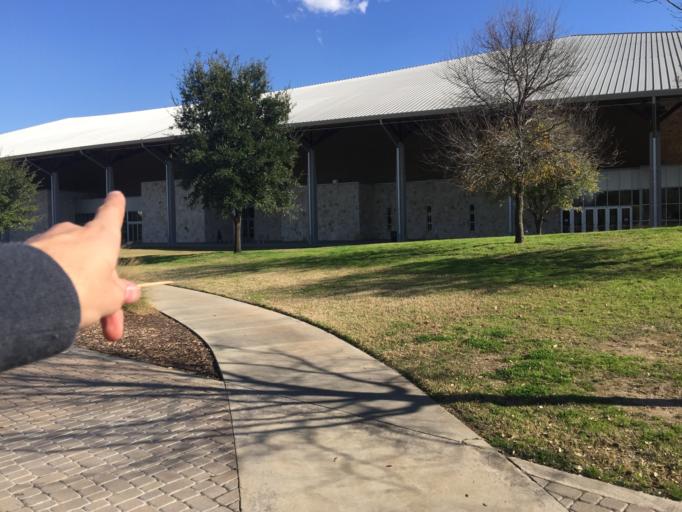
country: US
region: Texas
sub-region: Travis County
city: Austin
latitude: 30.2610
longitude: -97.7539
